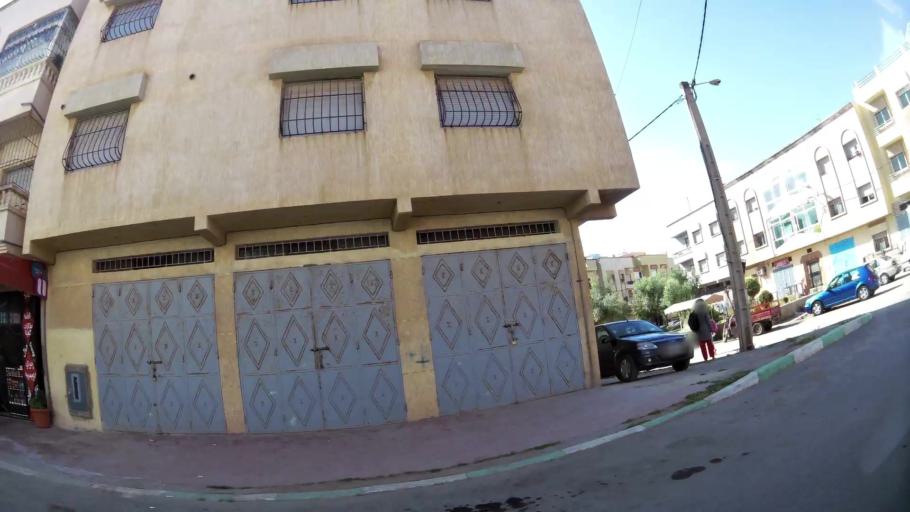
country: MA
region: Rabat-Sale-Zemmour-Zaer
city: Sale
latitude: 34.0556
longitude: -6.8131
